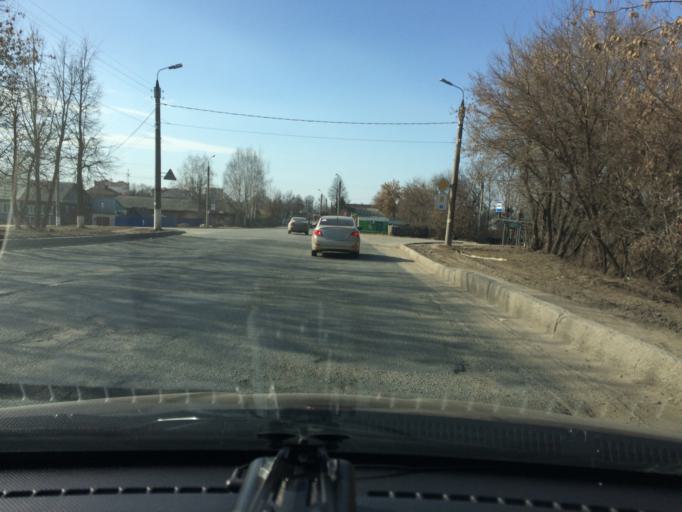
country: RU
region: Mariy-El
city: Yoshkar-Ola
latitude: 56.6447
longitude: 47.9106
